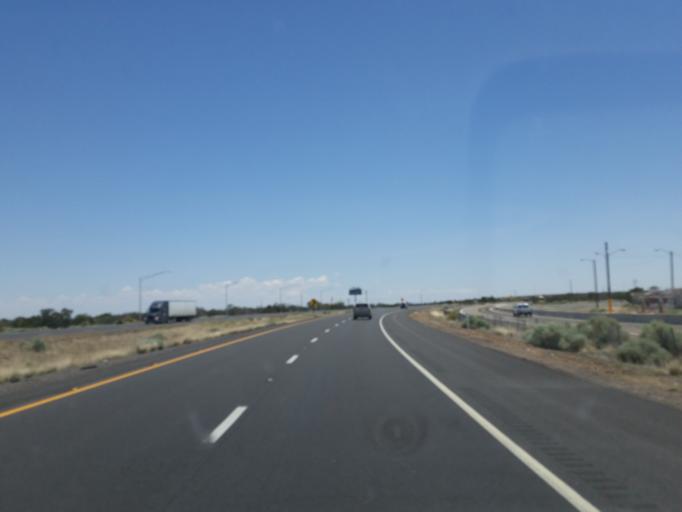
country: US
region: Arizona
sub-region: Coconino County
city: Flagstaff
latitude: 35.1612
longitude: -111.2806
